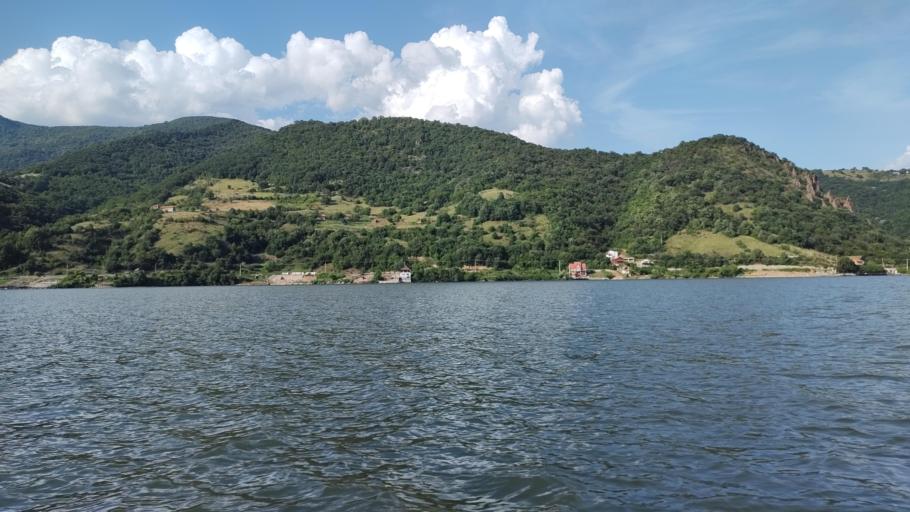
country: RO
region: Mehedinti
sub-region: Comuna Svinita
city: Svinita
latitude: 44.5384
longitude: 22.0563
